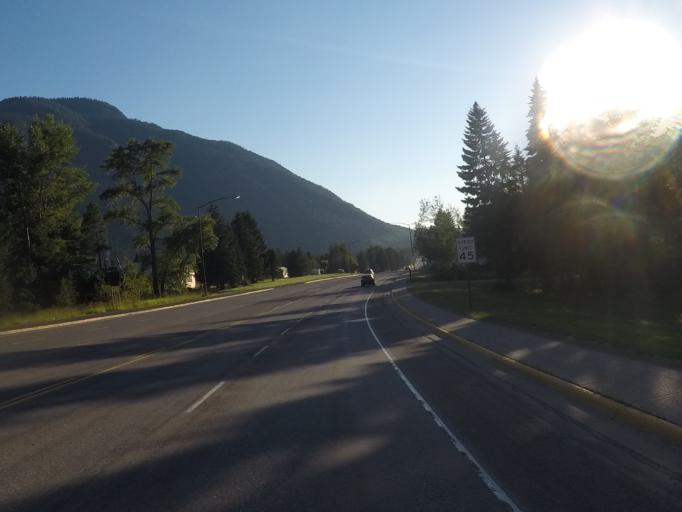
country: US
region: Montana
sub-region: Flathead County
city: Columbia Falls
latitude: 48.3859
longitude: -114.0542
